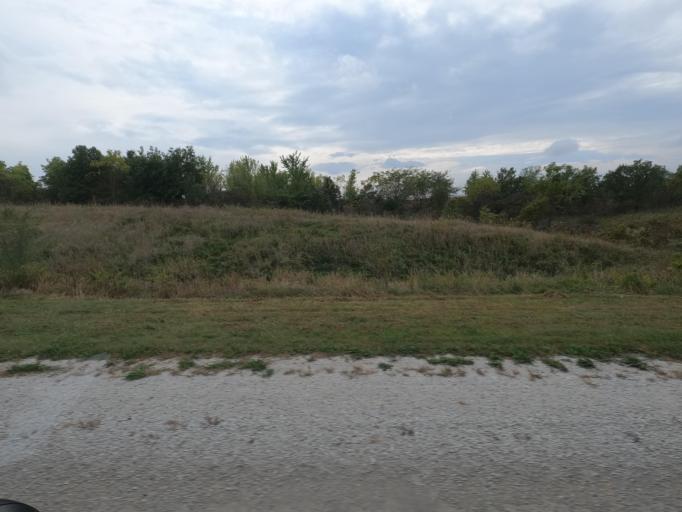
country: US
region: Iowa
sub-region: Wapello County
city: Ottumwa
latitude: 41.0663
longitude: -92.3915
